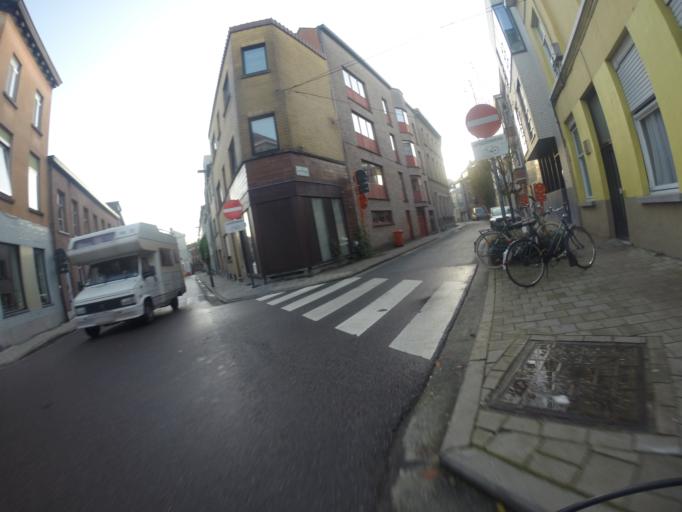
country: BE
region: Flanders
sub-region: Provincie Oost-Vlaanderen
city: Gent
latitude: 51.0513
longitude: 3.7060
